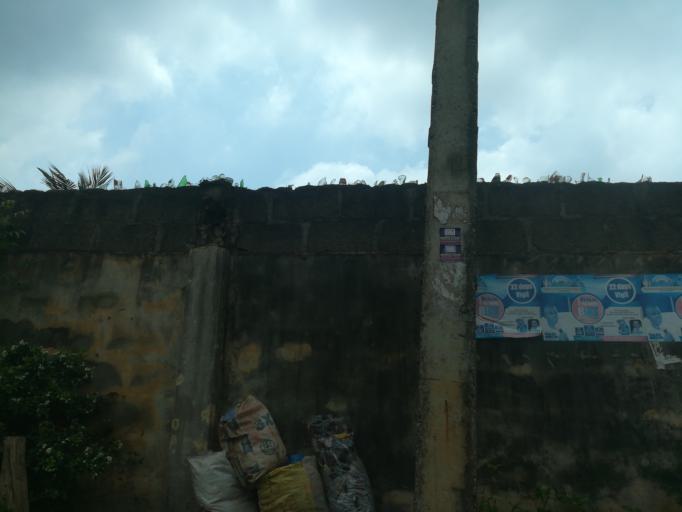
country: NG
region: Lagos
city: Ikorodu
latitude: 6.6168
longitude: 3.5209
